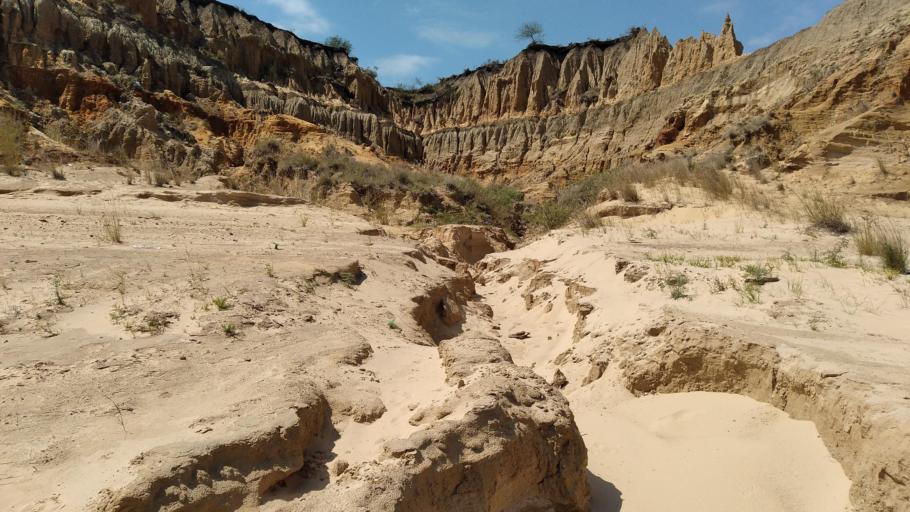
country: AR
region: Corrientes
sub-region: Departamento de Empedrado
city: Empedrado
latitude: -27.9422
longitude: -58.8115
